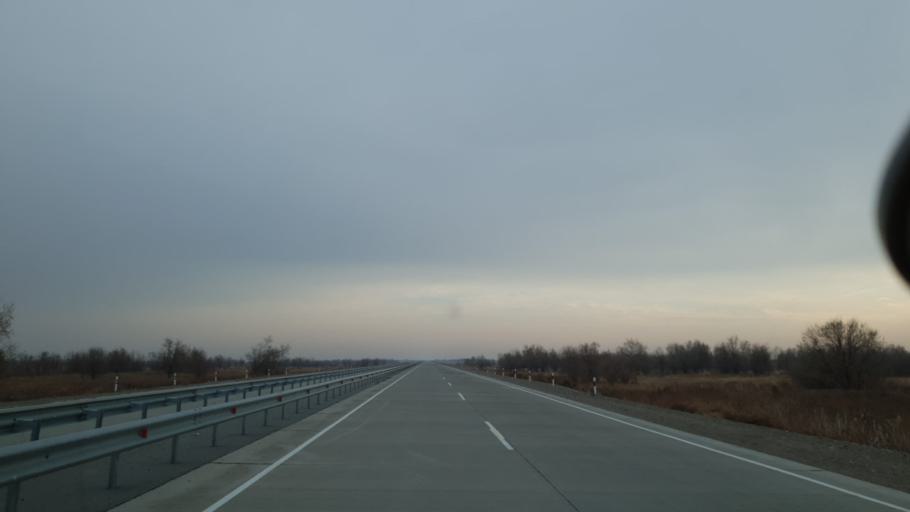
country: KZ
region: Almaty Oblysy
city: Zharkent
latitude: 44.0159
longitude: 79.7473
